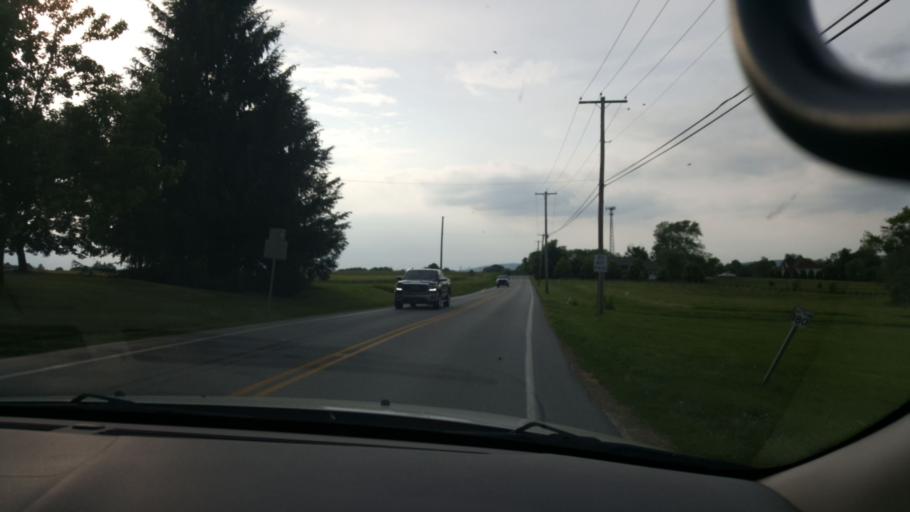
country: US
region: Pennsylvania
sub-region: York County
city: Shiloh
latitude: 39.9881
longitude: -76.7868
